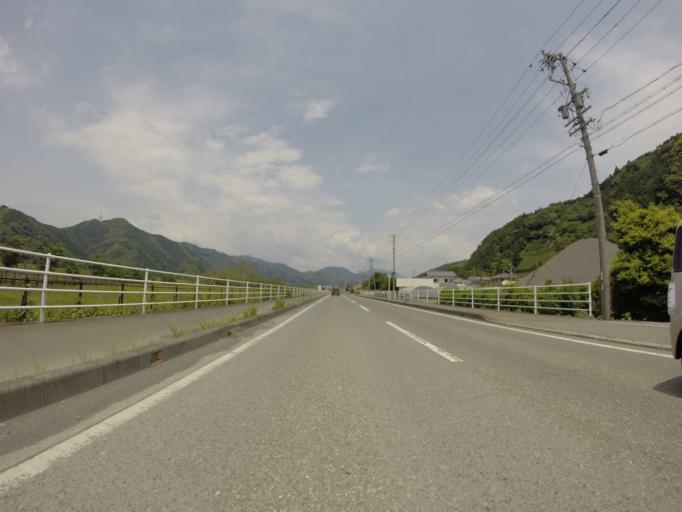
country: JP
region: Shizuoka
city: Shizuoka-shi
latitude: 35.0515
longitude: 138.3729
